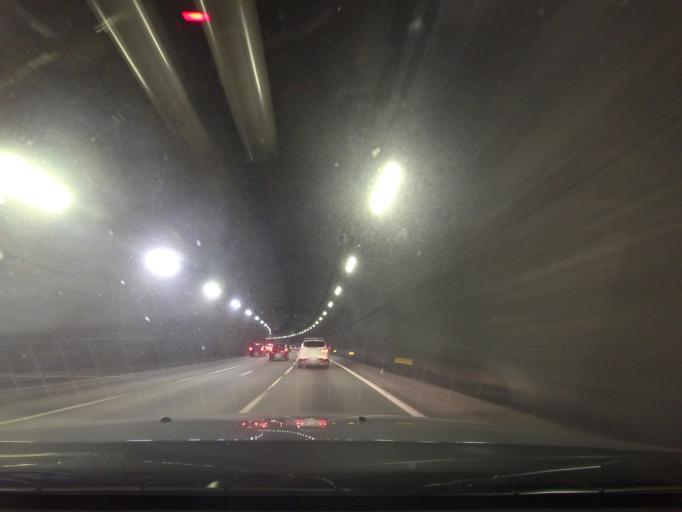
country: BR
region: Sao Paulo
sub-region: Cubatao
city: Cubatao
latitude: -23.8872
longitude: -46.5025
